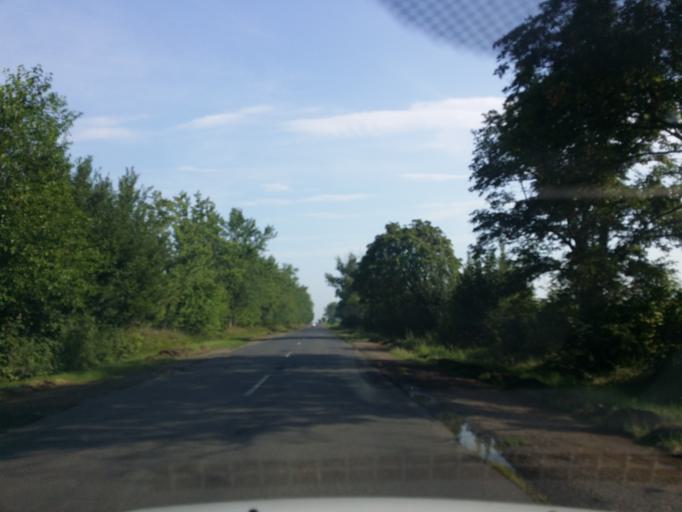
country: HU
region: Borsod-Abauj-Zemplen
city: Abaujszanto
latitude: 48.3591
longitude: 21.2154
